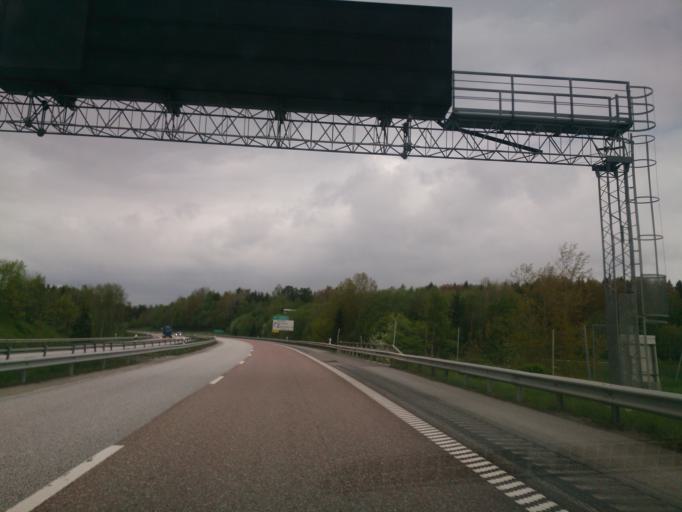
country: SE
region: Stockholm
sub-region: Sodertalje Kommun
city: Pershagen
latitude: 59.1452
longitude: 17.6502
